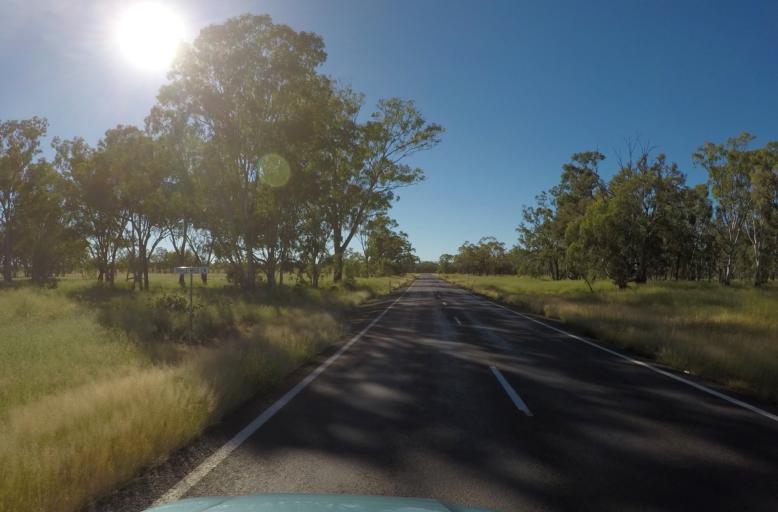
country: AU
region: Queensland
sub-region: Maranoa
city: Roma
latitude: -26.0845
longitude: 148.6289
